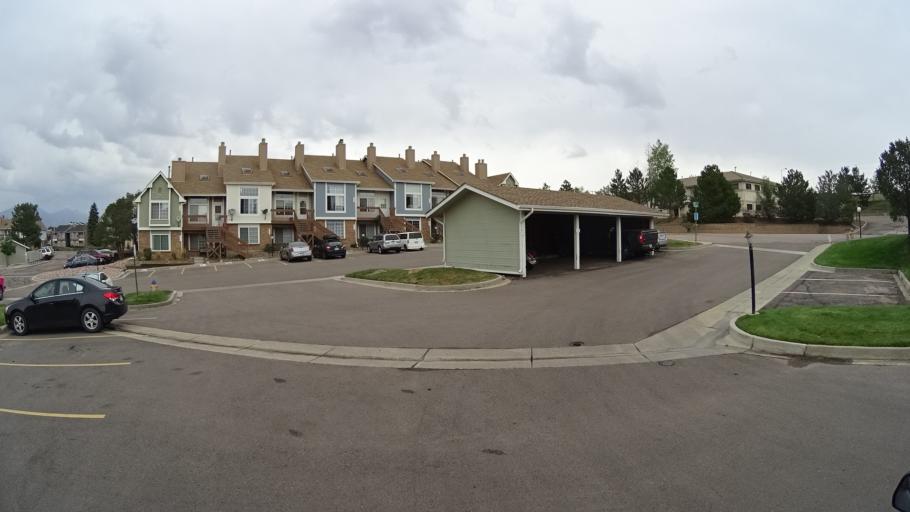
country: US
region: Colorado
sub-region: El Paso County
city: Colorado Springs
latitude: 38.9241
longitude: -104.7951
